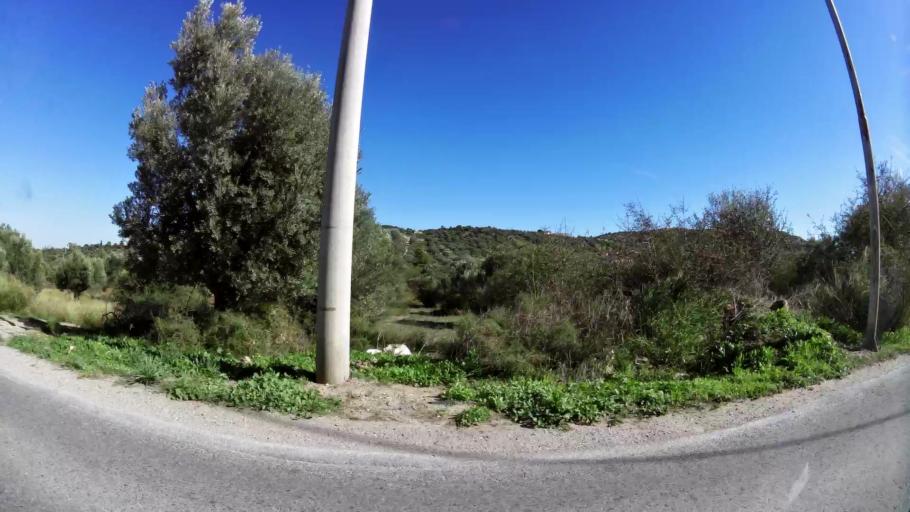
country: GR
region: Attica
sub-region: Nomarchia Anatolikis Attikis
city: Paiania
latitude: 37.9705
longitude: 23.8625
